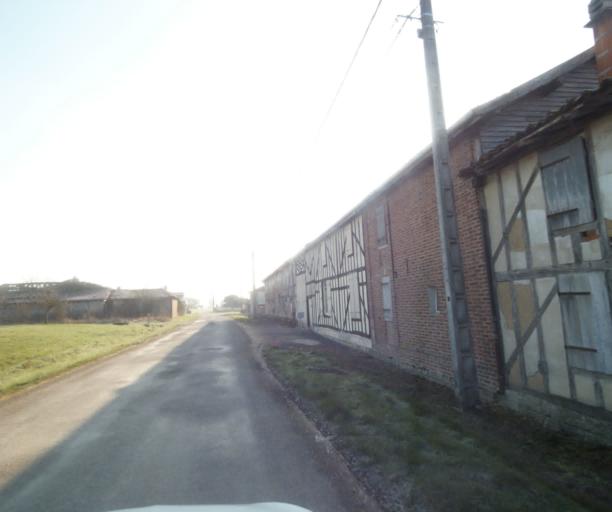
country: FR
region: Champagne-Ardenne
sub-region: Departement de la Haute-Marne
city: Montier-en-Der
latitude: 48.5028
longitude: 4.7289
